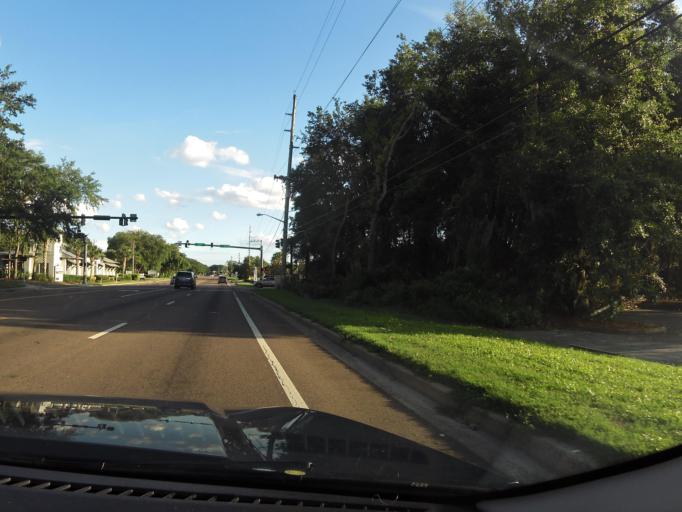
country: US
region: Florida
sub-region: Nassau County
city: Fernandina Beach
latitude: 30.6464
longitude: -81.4551
